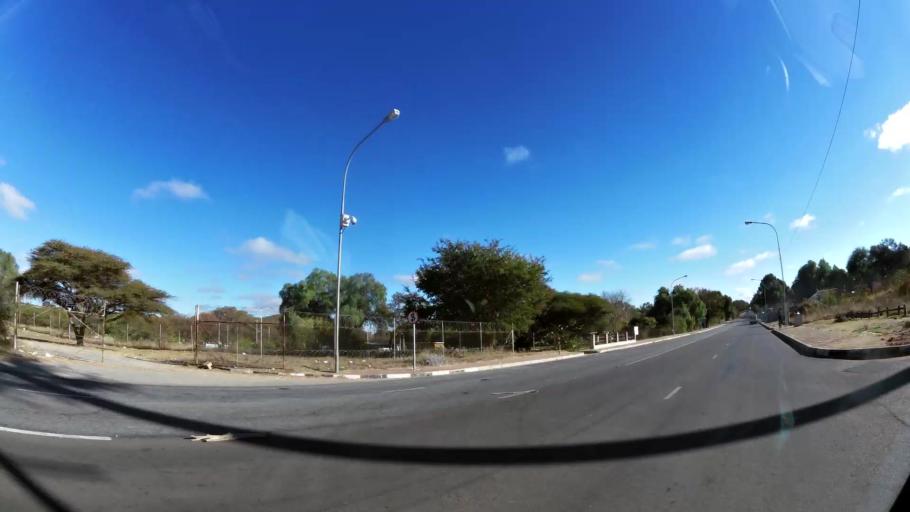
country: ZA
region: Limpopo
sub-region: Capricorn District Municipality
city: Polokwane
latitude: -23.9216
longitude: 29.4628
